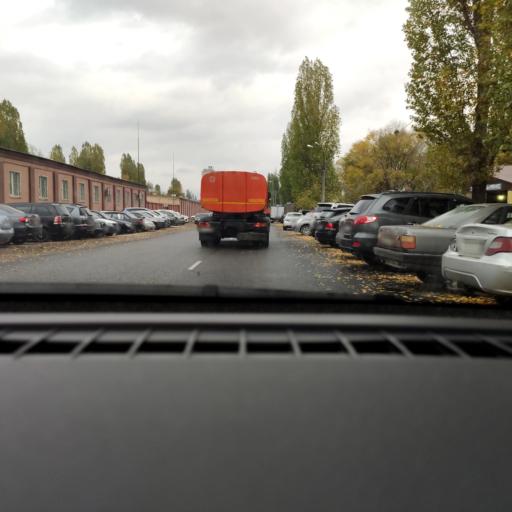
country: RU
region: Voronezj
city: Voronezh
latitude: 51.6771
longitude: 39.2644
